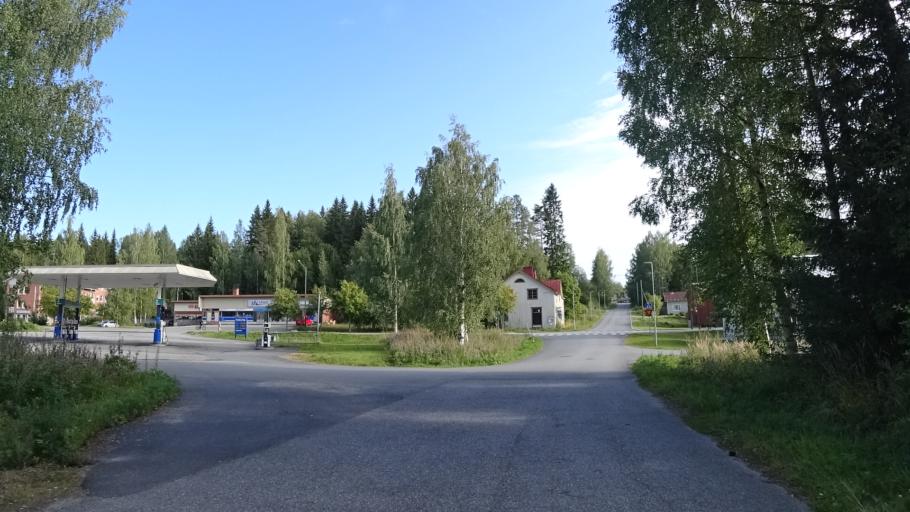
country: FI
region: North Karelia
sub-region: Joensuu
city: Eno
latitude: 62.7990
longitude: 30.1506
